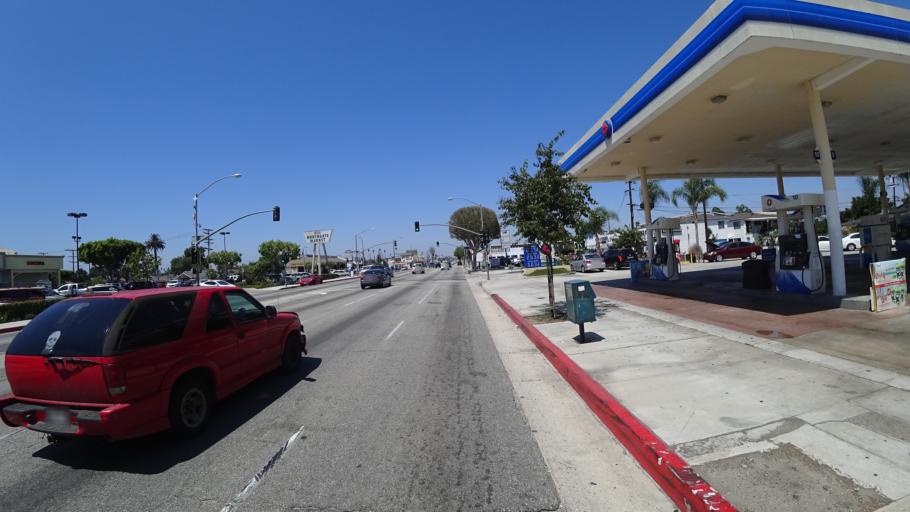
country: US
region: California
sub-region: Los Angeles County
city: Lennox
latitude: 33.9373
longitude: -118.3438
